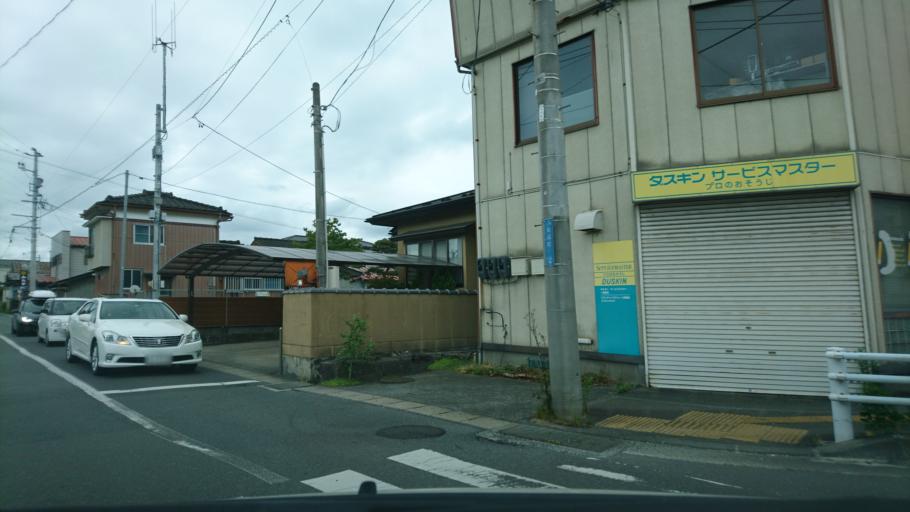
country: JP
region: Iwate
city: Ichinoseki
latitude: 38.9226
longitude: 141.1345
